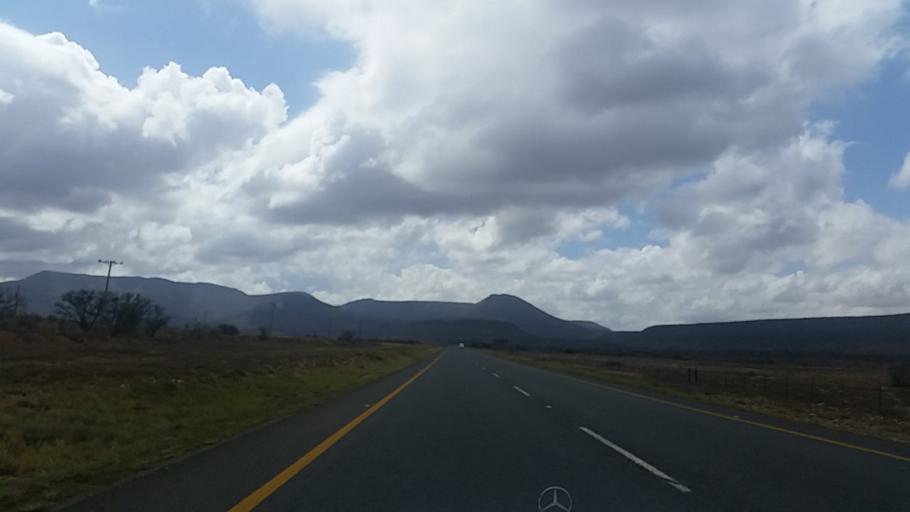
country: ZA
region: Eastern Cape
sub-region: Cacadu District Municipality
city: Graaff-Reinet
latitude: -32.0965
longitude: 24.6045
